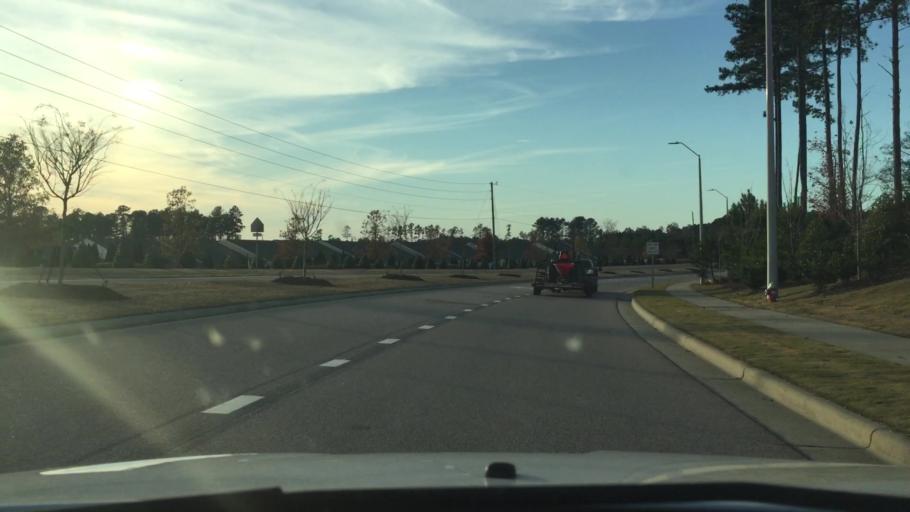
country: US
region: North Carolina
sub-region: Wake County
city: Green Level
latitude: 35.8431
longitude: -78.9107
